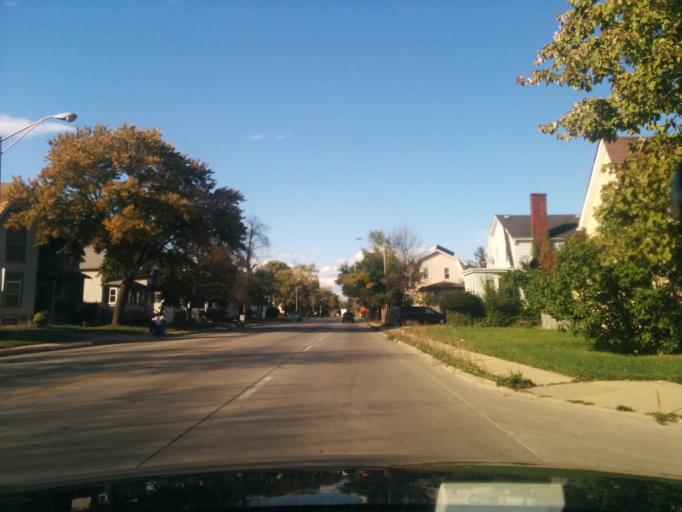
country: US
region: Illinois
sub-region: Cook County
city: Maywood
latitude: 41.8900
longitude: -87.8344
